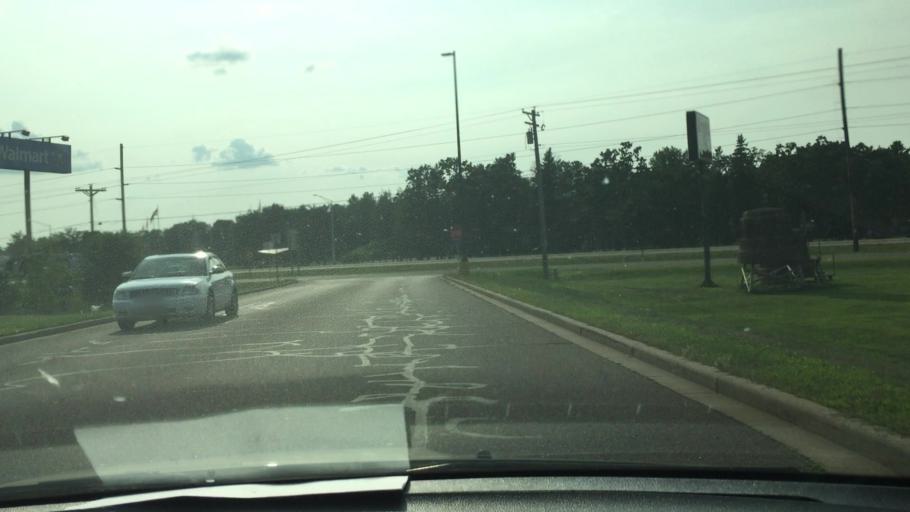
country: US
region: Wisconsin
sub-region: Chippewa County
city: Lake Hallie
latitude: 44.8840
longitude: -91.4243
